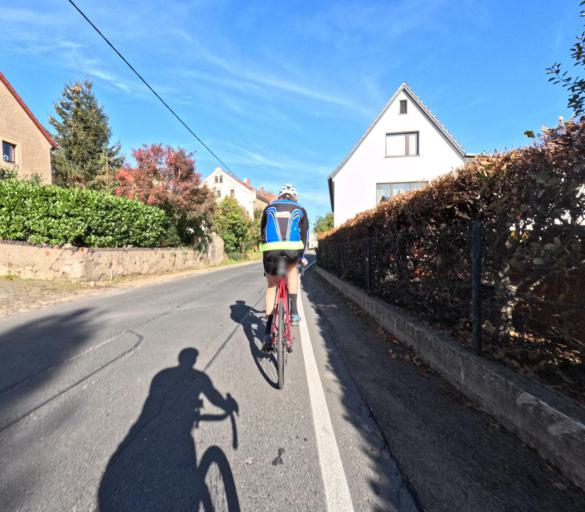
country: DE
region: Saxony
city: Ottendorf-Okrilla
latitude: 51.1312
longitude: 13.8393
